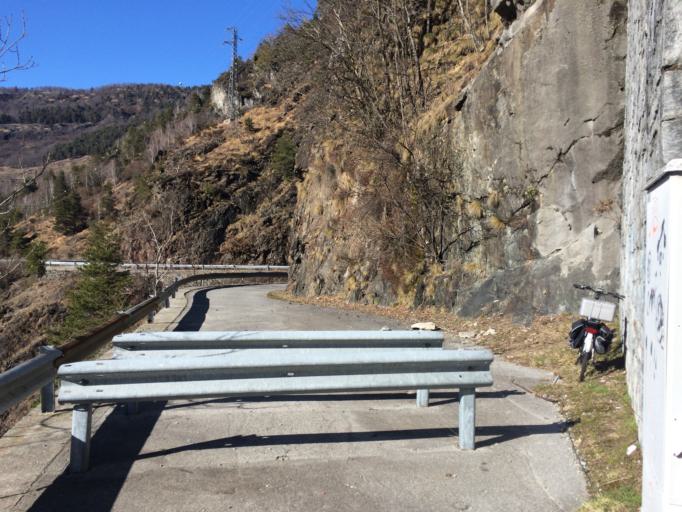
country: IT
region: Piedmont
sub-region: Provincia Verbano-Cusio-Ossola
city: Cursolo
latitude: 46.1001
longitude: 8.5502
